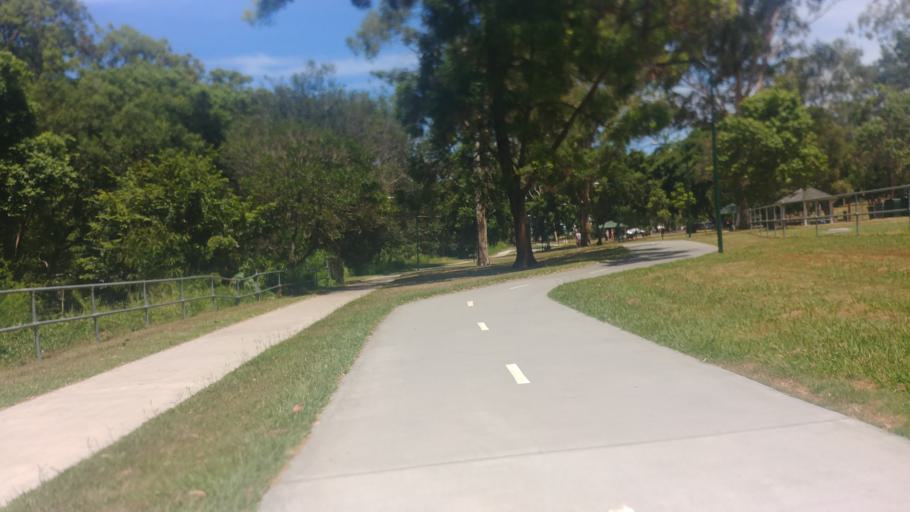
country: AU
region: Queensland
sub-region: Brisbane
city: Wavell Heights
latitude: -27.4051
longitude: 153.0512
